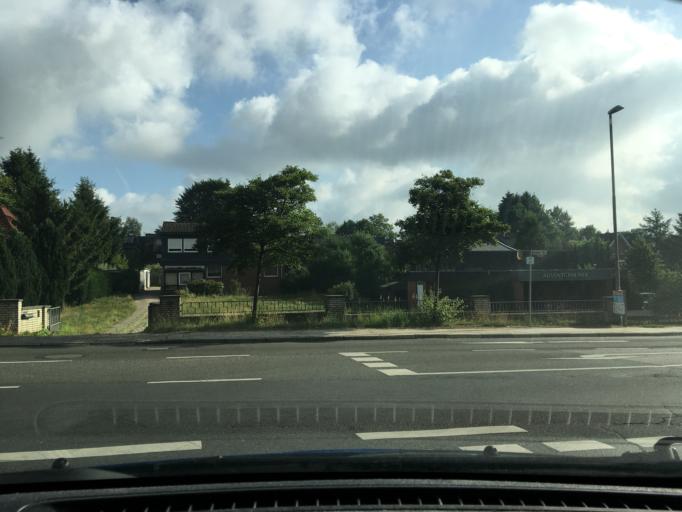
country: DE
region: Lower Saxony
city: Buchholz in der Nordheide
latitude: 53.3237
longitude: 9.8544
